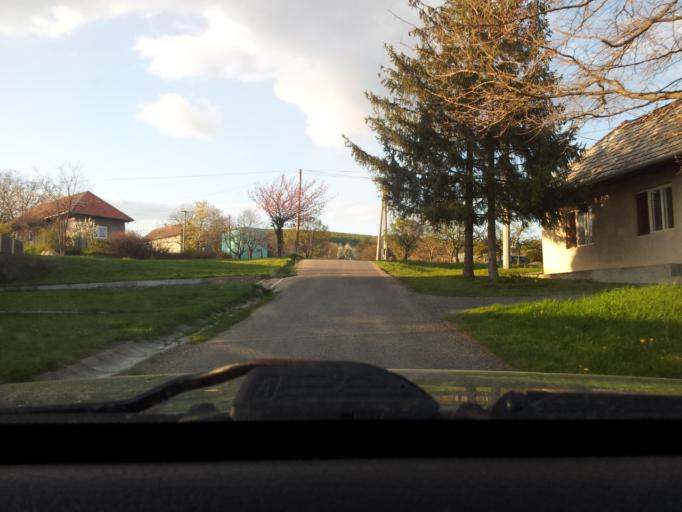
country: SK
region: Nitriansky
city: Tlmace
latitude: 48.2973
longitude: 18.5620
